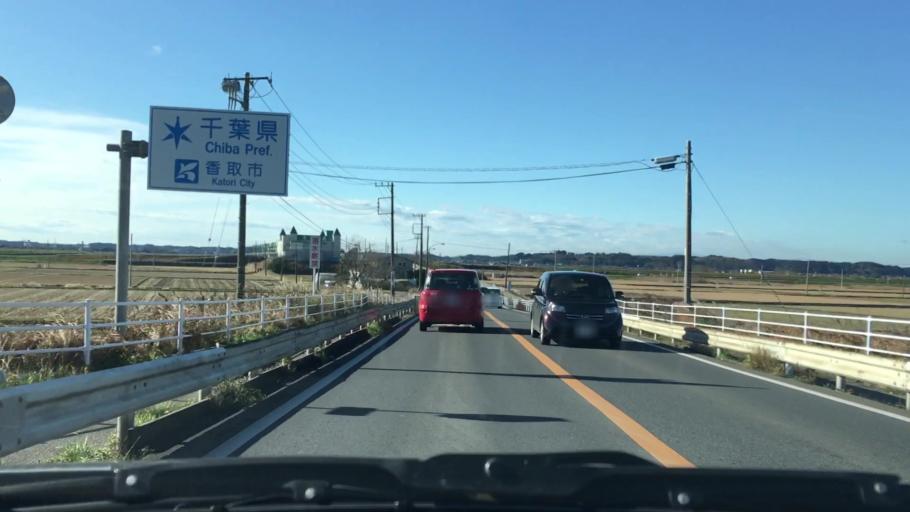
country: JP
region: Chiba
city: Omigawa
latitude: 35.8723
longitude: 140.6218
